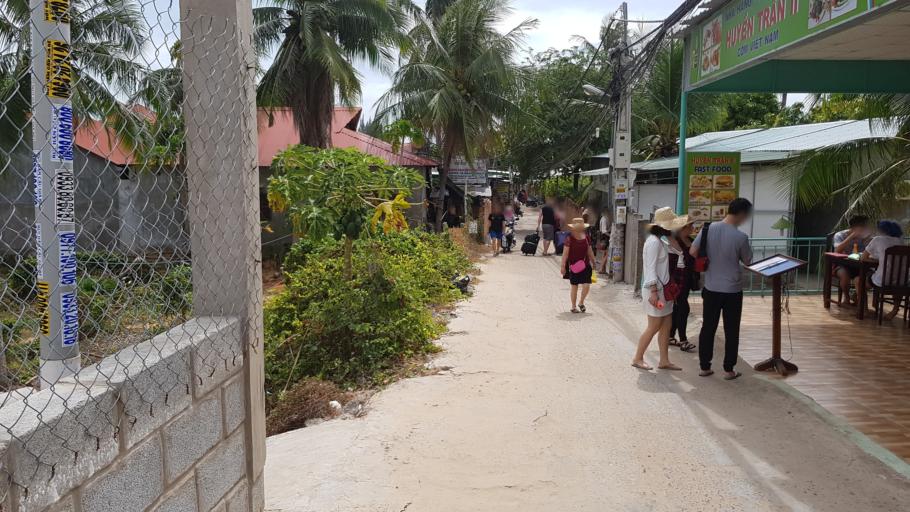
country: VN
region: Binh Thuan
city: Phan Thiet
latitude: 10.9486
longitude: 108.2002
